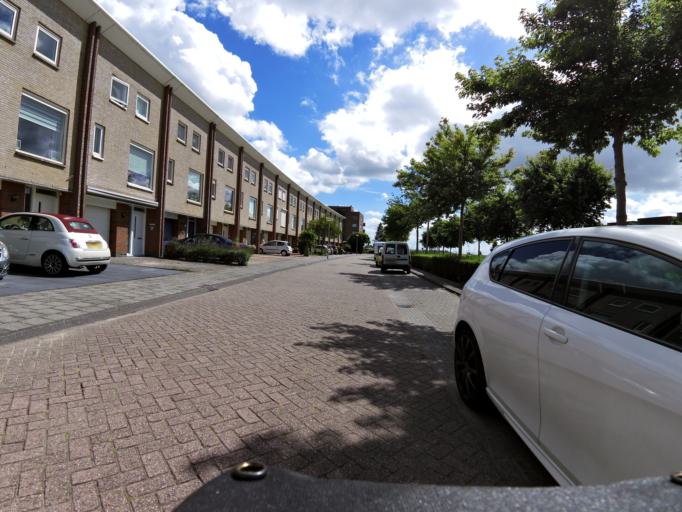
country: NL
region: South Holland
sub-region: Gemeente Oud-Beijerland
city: Oud-Beijerland
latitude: 51.8291
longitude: 4.3711
